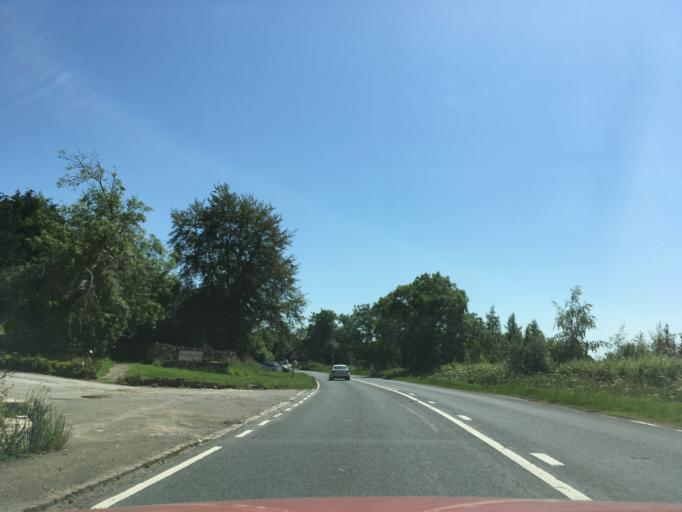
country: GB
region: England
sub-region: Oxfordshire
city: Chipping Norton
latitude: 51.9577
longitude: -1.6086
